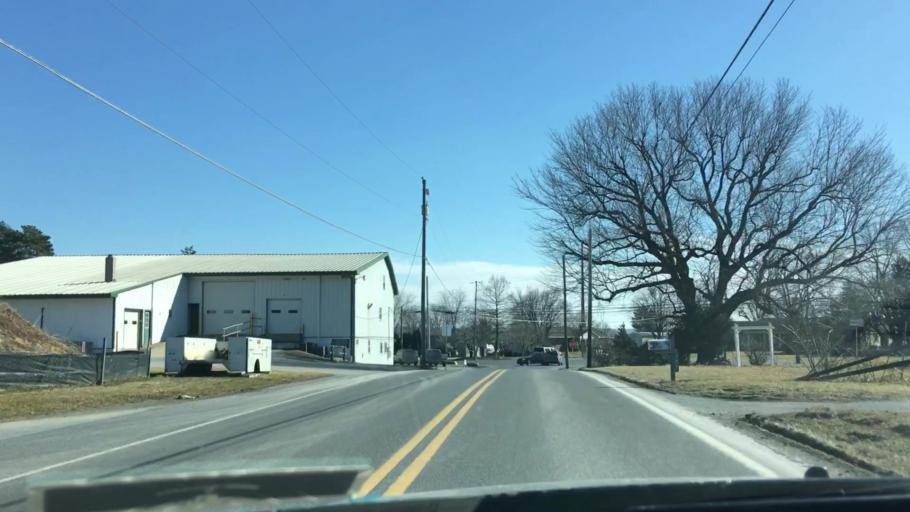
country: US
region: Pennsylvania
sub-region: Lancaster County
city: Reamstown
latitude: 40.1720
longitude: -76.1246
